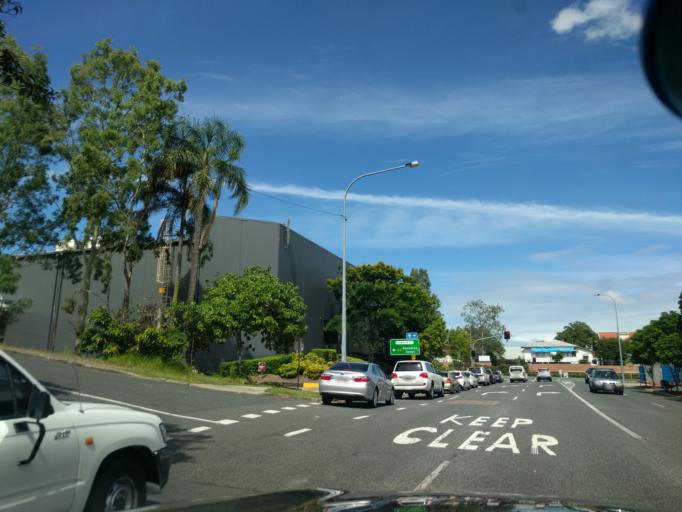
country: AU
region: Queensland
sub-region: Brisbane
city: Windsor
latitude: -27.4379
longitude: 153.0300
